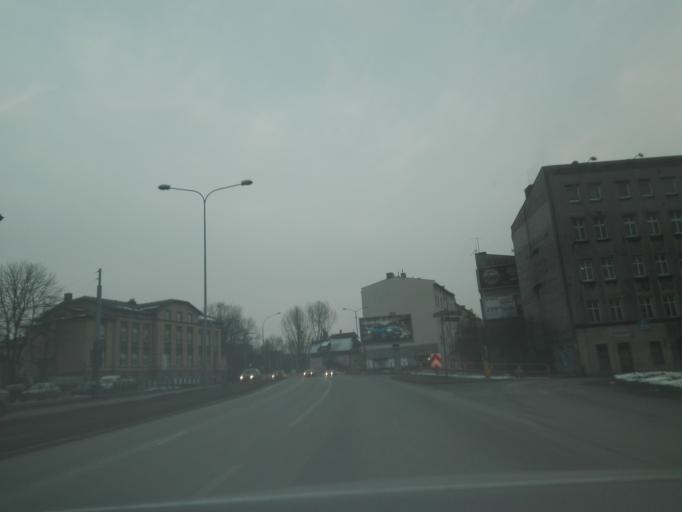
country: PL
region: Silesian Voivodeship
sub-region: Chorzow
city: Chorzow
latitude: 50.2949
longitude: 18.9564
